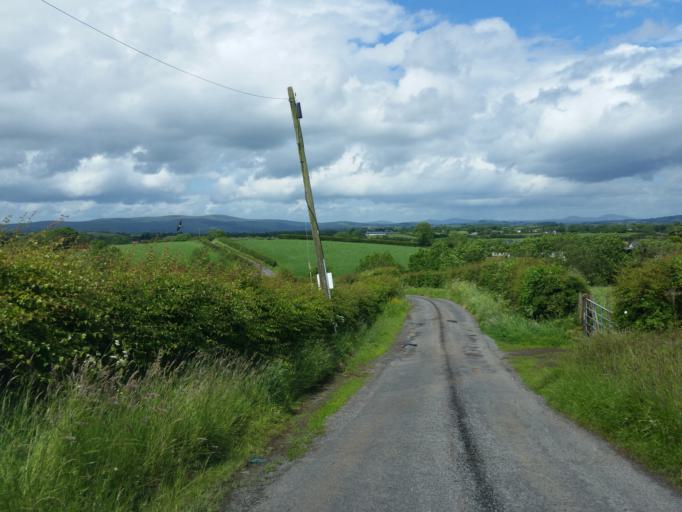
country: GB
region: Northern Ireland
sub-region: Omagh District
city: Omagh
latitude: 54.5423
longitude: -7.1346
